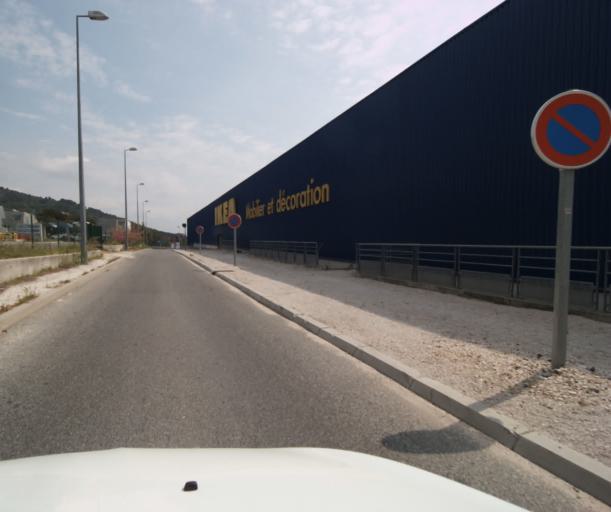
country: FR
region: Provence-Alpes-Cote d'Azur
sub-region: Departement du Var
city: La Garde
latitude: 43.1424
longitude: 6.0106
